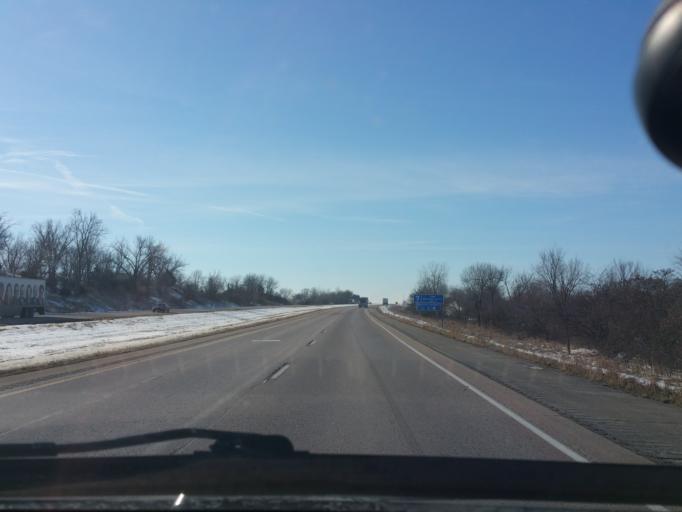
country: US
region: Iowa
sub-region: Decatur County
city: Lamoni
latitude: 40.6471
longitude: -93.8655
